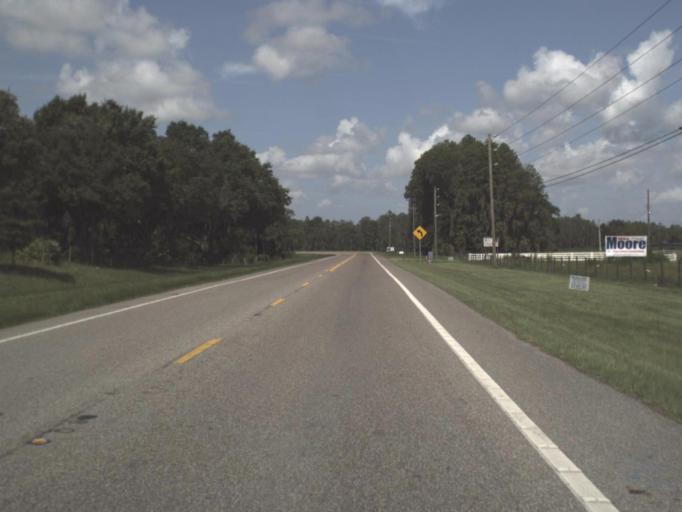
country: US
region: Florida
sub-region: Pasco County
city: Shady Hills
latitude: 28.3253
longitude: -82.4880
